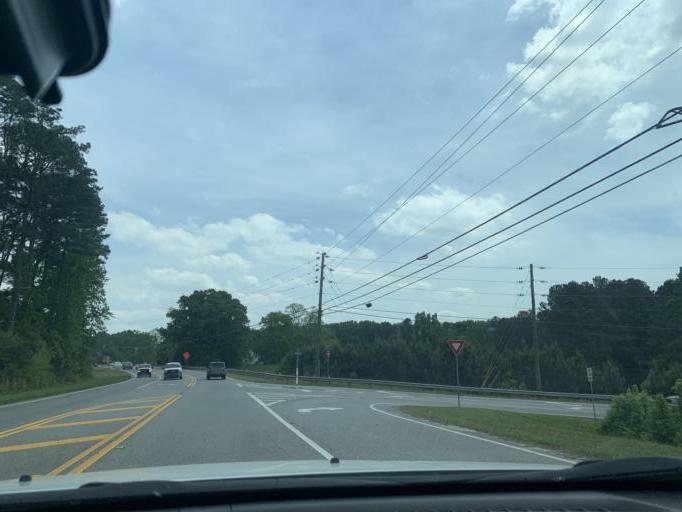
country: US
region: Georgia
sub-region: Forsyth County
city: Cumming
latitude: 34.1514
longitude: -84.1523
